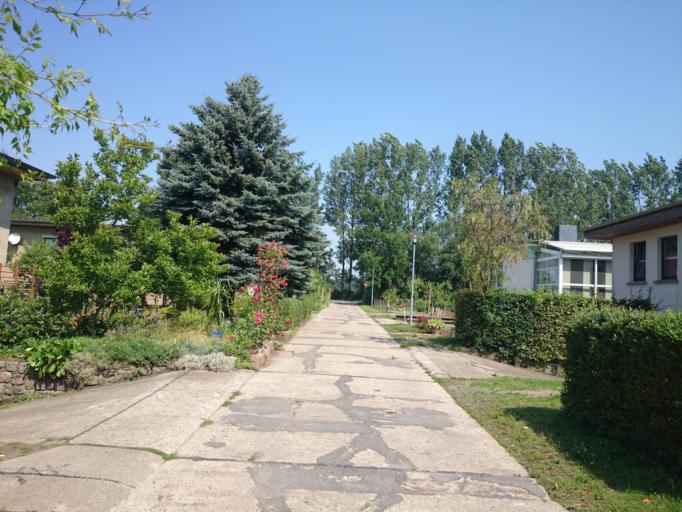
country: DE
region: Mecklenburg-Vorpommern
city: Broderstorf
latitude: 54.0730
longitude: 12.3475
